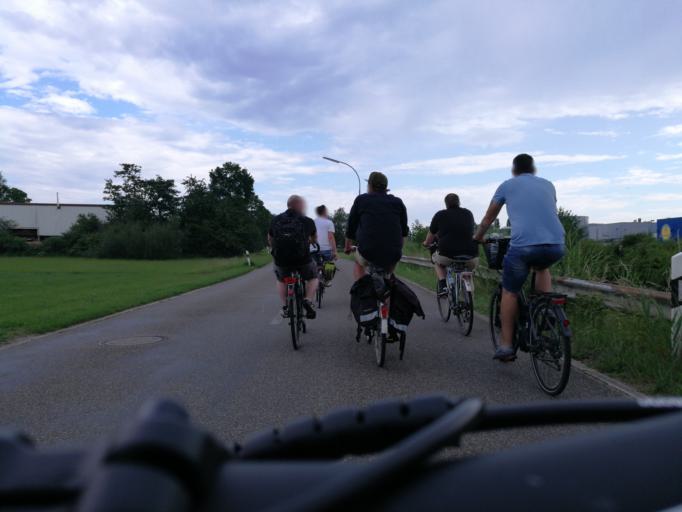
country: DE
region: North Rhine-Westphalia
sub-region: Regierungsbezirk Dusseldorf
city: Kleve
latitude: 51.8102
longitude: 6.1447
